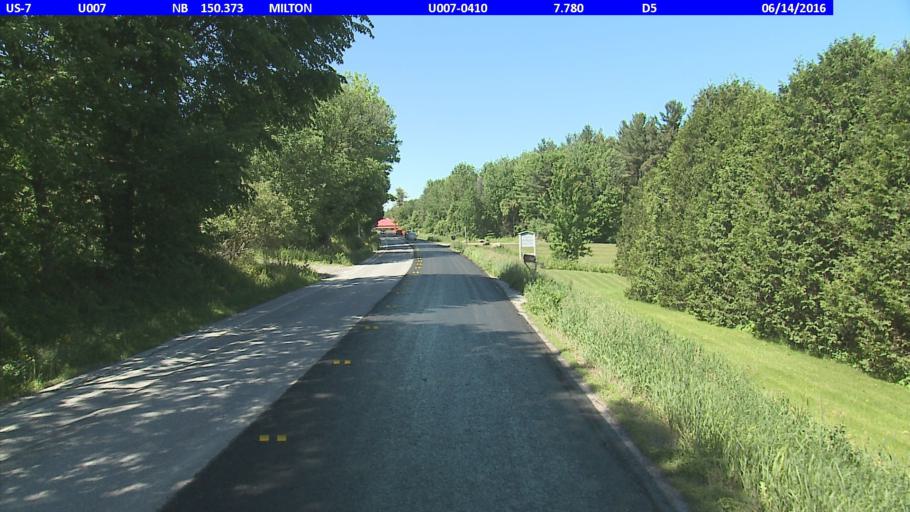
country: US
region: Vermont
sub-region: Chittenden County
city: Milton
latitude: 44.6785
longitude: -73.1110
